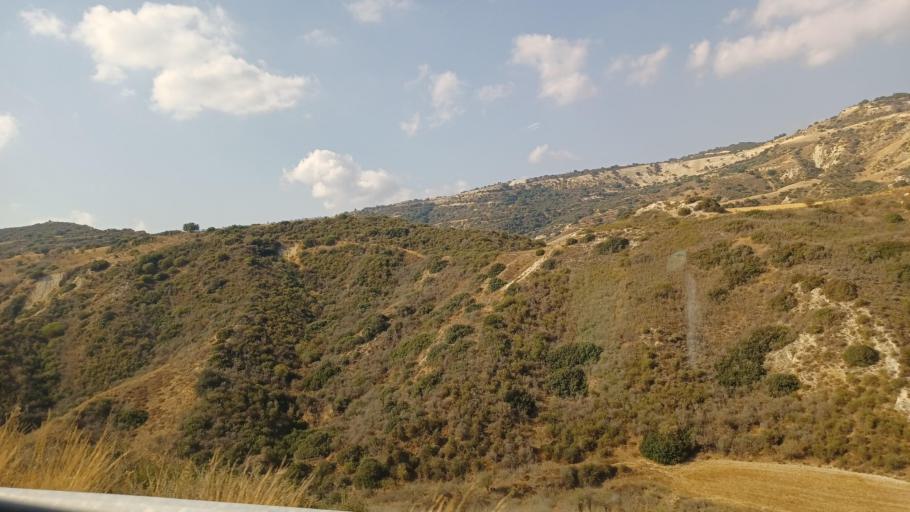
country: CY
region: Pafos
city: Polis
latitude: 34.9962
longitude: 32.4316
